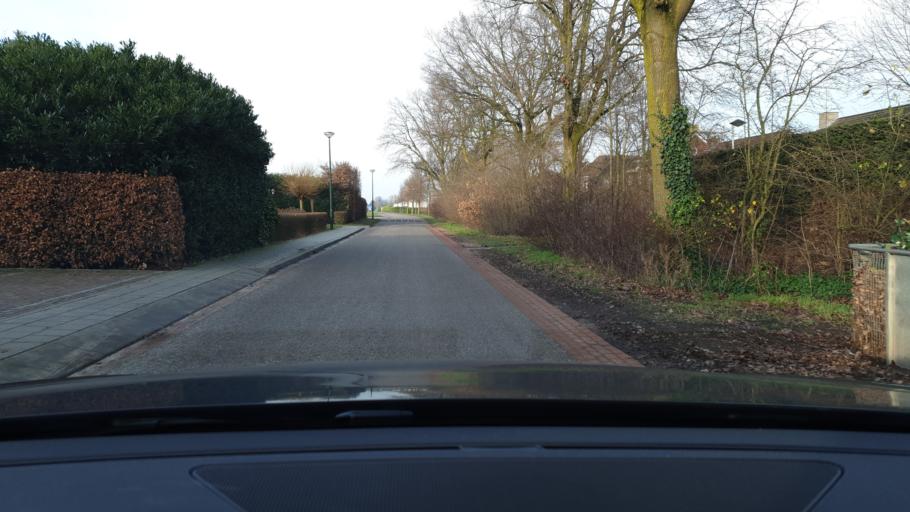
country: NL
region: Limburg
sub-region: Gemeente Venray
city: Venray
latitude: 51.4591
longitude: 6.0396
